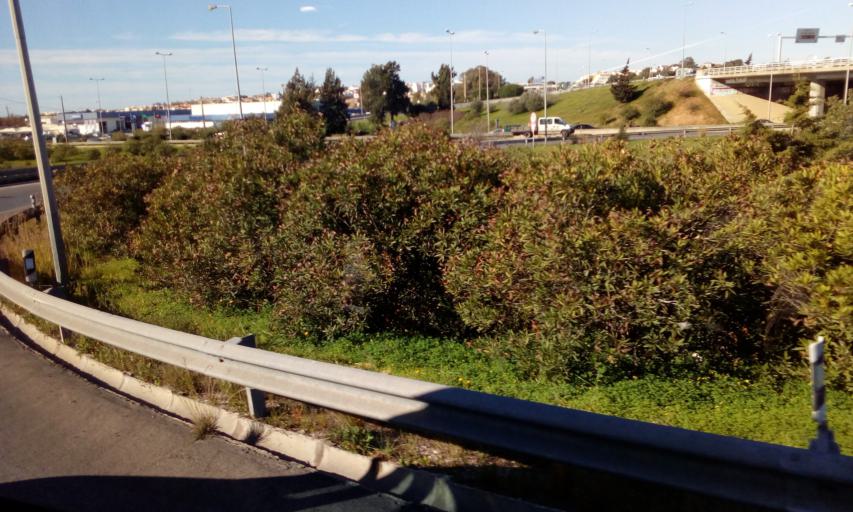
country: PT
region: Faro
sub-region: Faro
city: Faro
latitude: 37.0397
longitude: -7.9490
